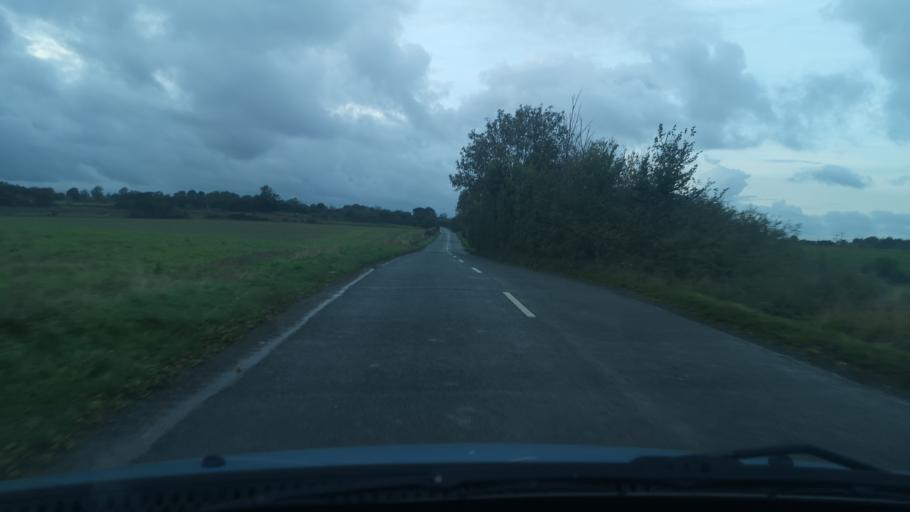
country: GB
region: England
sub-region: Doncaster
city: Norton
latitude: 53.6363
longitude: -1.2056
